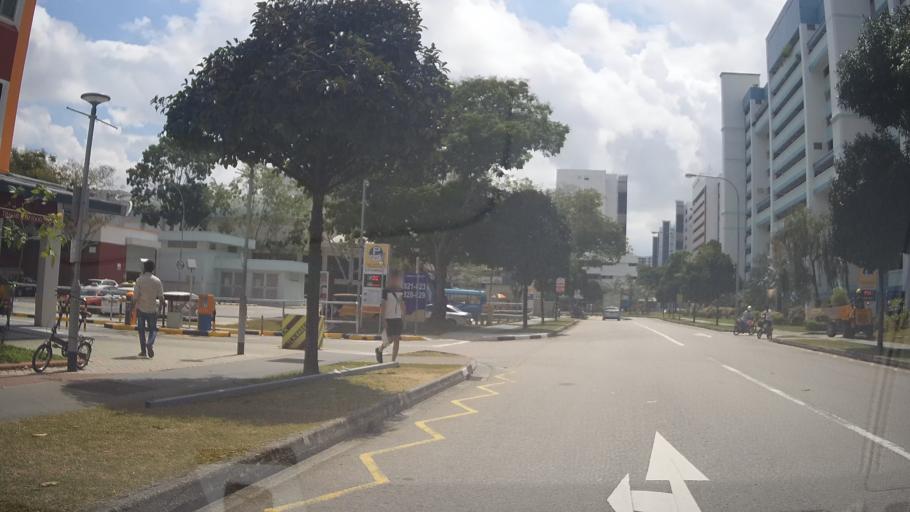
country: SG
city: Singapore
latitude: 1.3482
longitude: 103.9344
